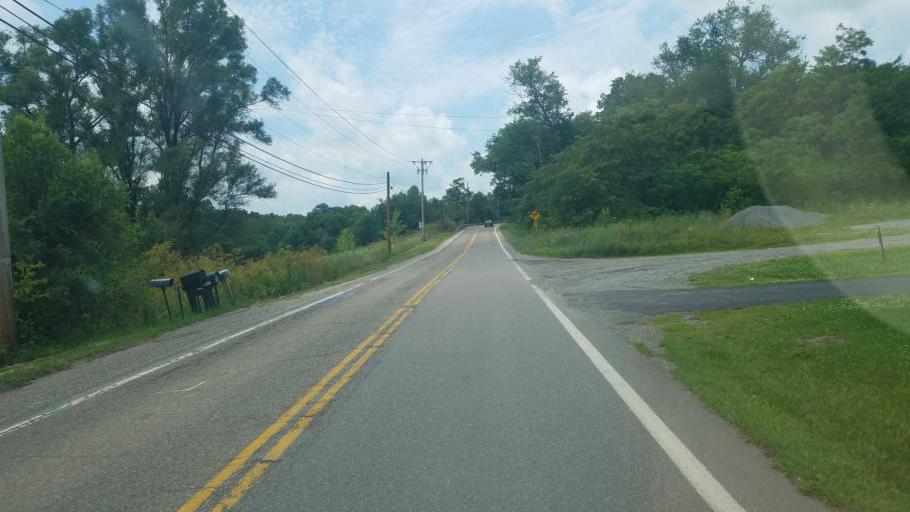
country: US
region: Ohio
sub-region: Columbiana County
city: Lisbon
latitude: 40.7623
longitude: -80.7052
